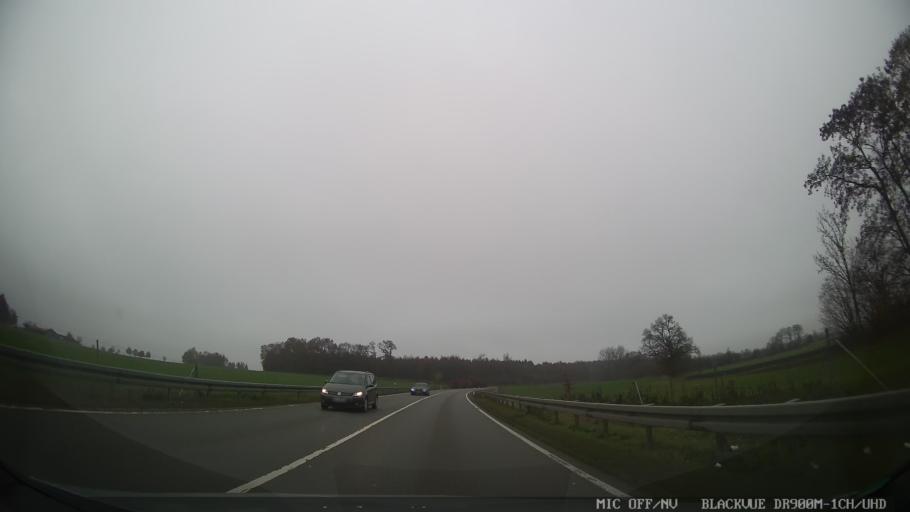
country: DE
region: Bavaria
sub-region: Upper Bavaria
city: Poing
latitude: 48.1625
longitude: 11.8308
